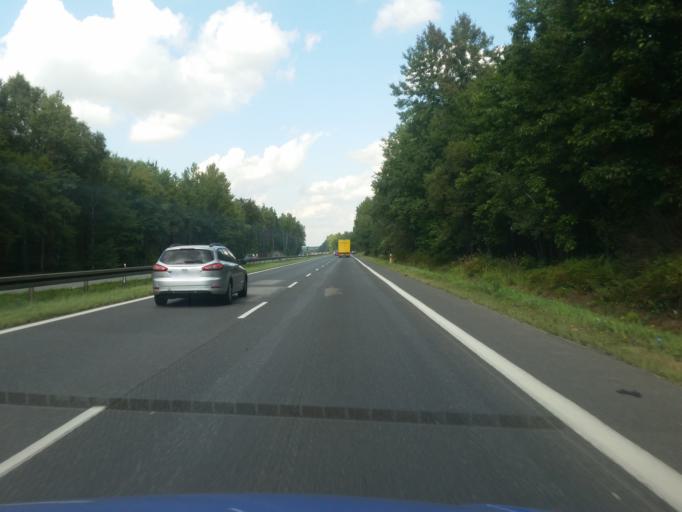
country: PL
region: Silesian Voivodeship
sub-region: Powiat bedzinski
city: Siewierz
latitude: 50.5222
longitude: 19.1932
